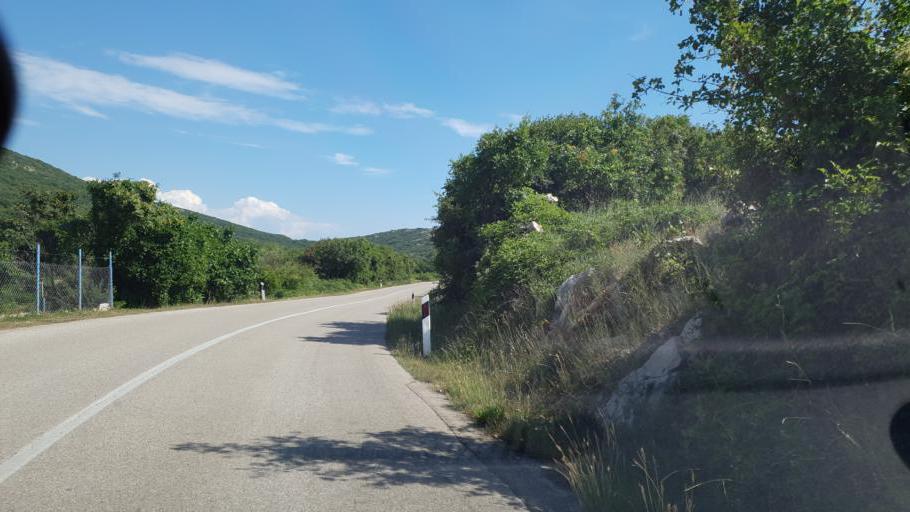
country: HR
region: Primorsko-Goranska
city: Punat
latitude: 45.0004
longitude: 14.6344
